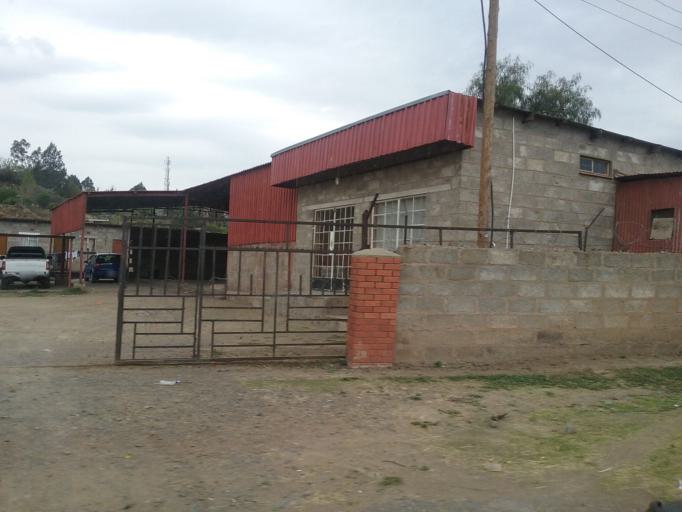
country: LS
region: Maseru
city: Maseru
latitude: -29.3297
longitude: 27.5066
